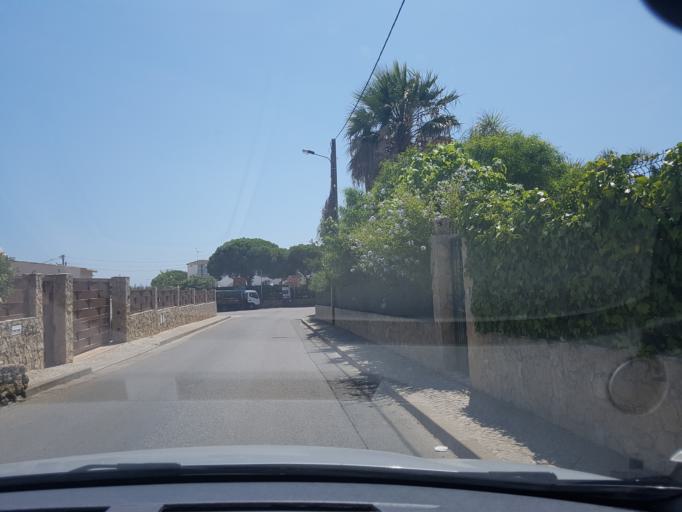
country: PT
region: Faro
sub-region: Lagoa
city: Carvoeiro
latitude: 37.0956
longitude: -8.4626
